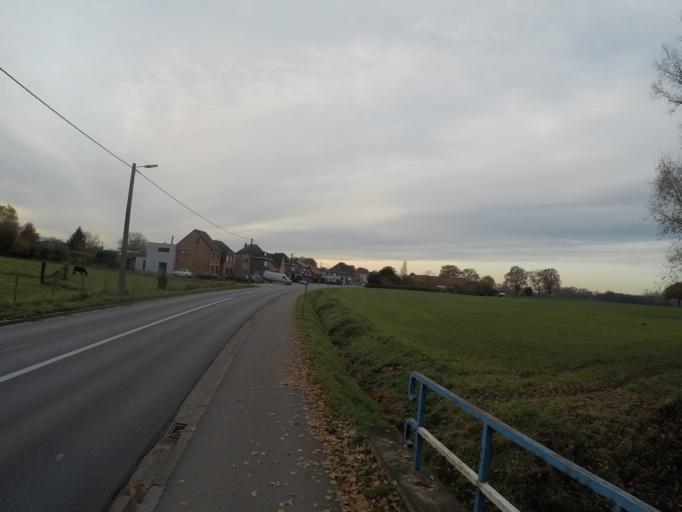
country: BE
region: Flanders
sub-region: Provincie Antwerpen
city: Berlaar
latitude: 51.1083
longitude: 4.6807
